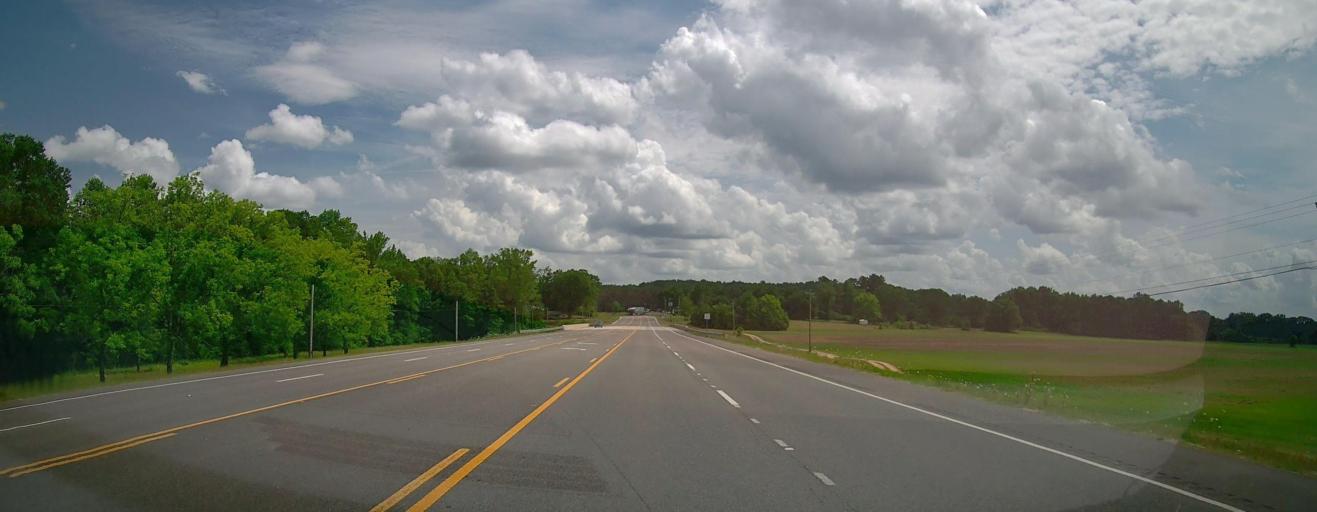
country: US
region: Alabama
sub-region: Marion County
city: Hamilton
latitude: 34.1050
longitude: -87.9891
